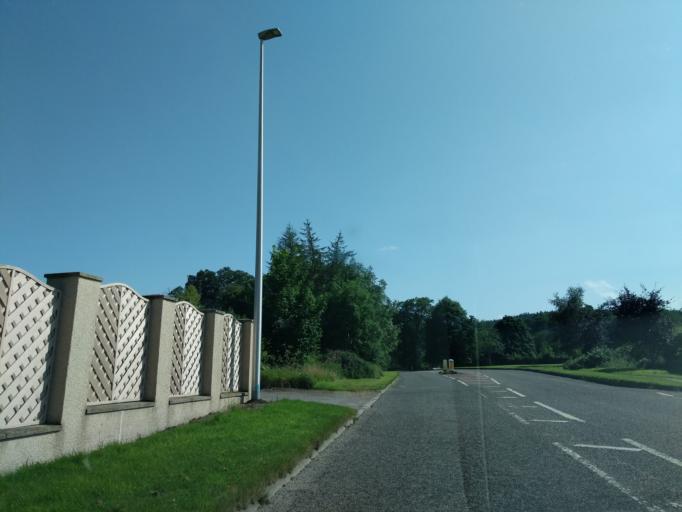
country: GB
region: Scotland
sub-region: Moray
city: Fochabers
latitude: 57.6102
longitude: -3.0889
